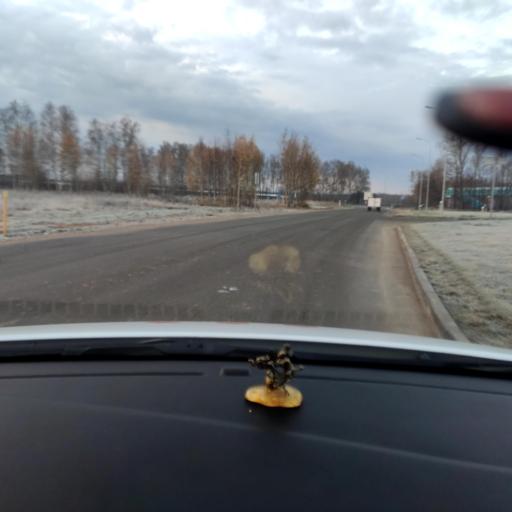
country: RU
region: Tatarstan
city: Osinovo
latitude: 55.8618
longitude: 48.8353
